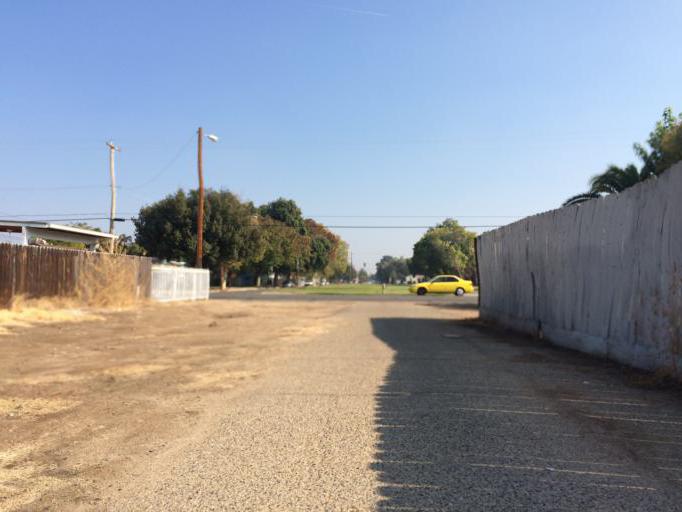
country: US
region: California
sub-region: Fresno County
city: Fresno
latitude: 36.7468
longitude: -119.7459
